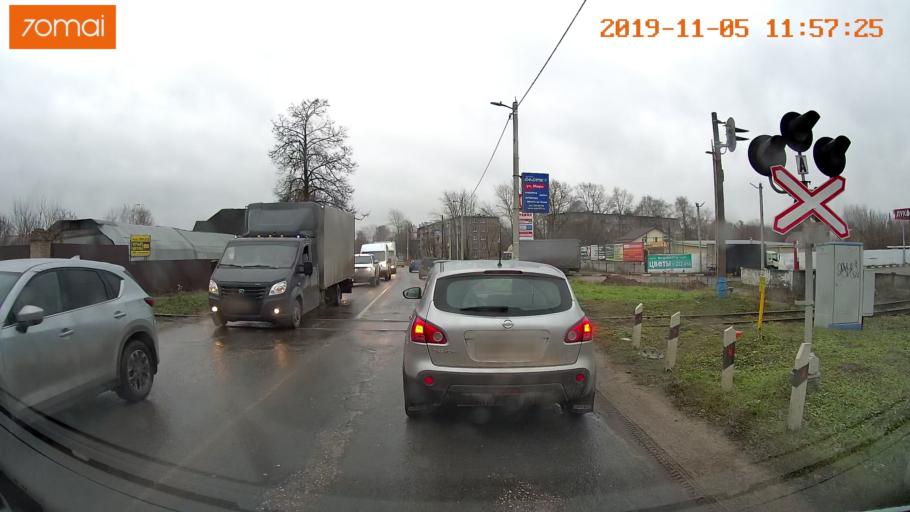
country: RU
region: Ivanovo
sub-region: Gorod Ivanovo
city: Ivanovo
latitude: 56.9832
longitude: 41.0345
